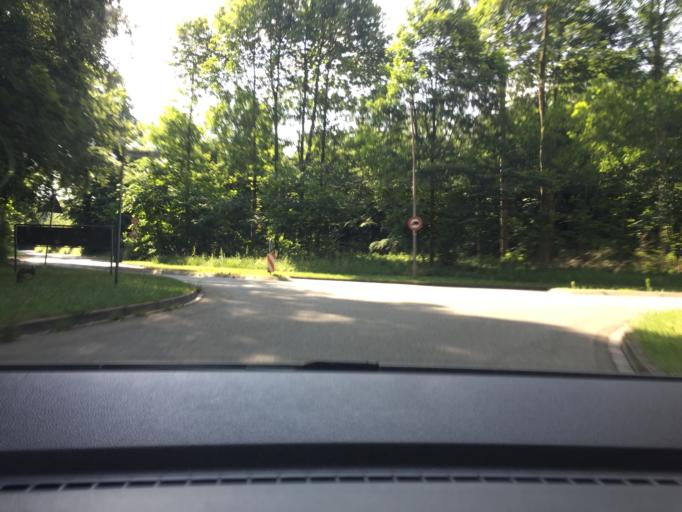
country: DE
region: Schleswig-Holstein
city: Itzehoe
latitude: 53.9411
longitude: 9.5328
